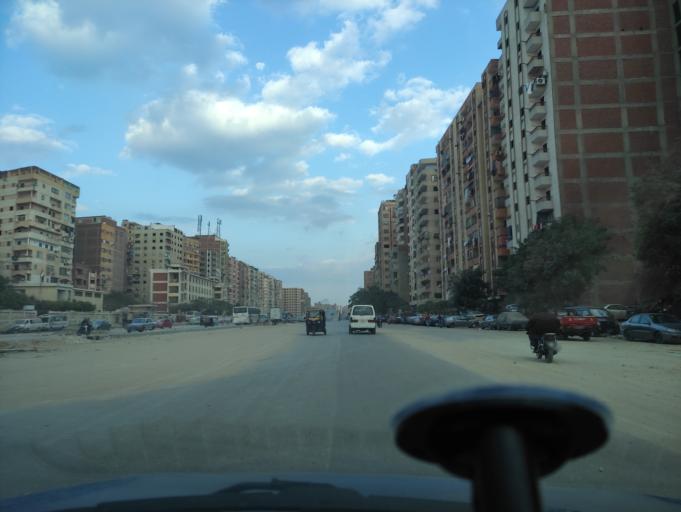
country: EG
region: Muhafazat al Qalyubiyah
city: Al Khankah
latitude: 30.1360
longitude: 31.3339
